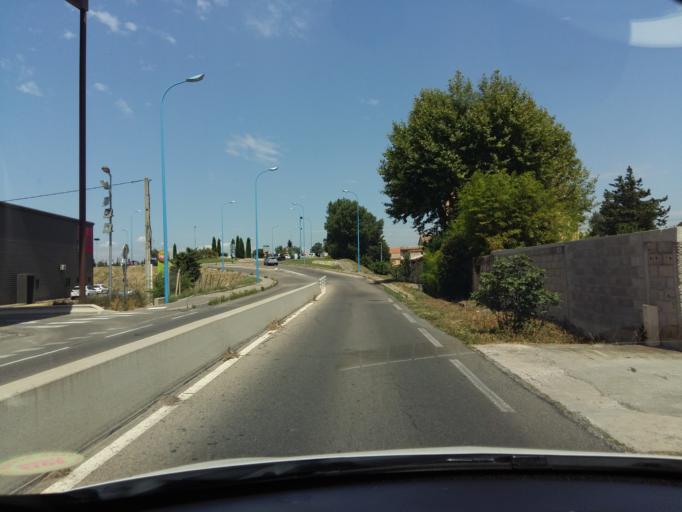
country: FR
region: Provence-Alpes-Cote d'Azur
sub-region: Departement du Vaucluse
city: Le Pontet
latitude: 43.9722
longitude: 4.8676
